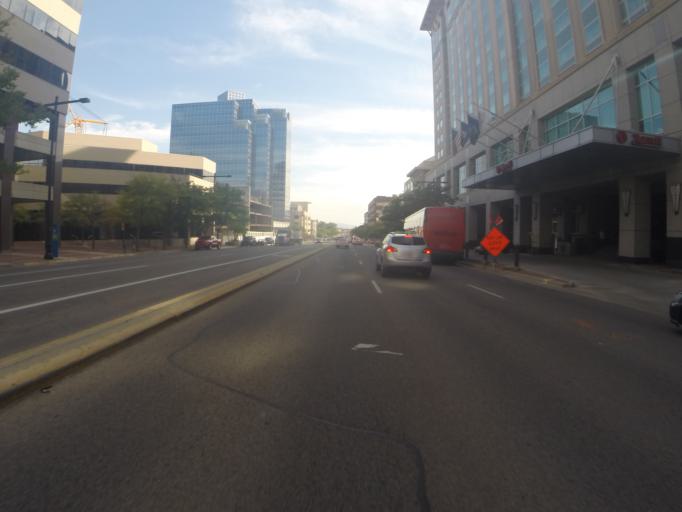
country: US
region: Utah
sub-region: Salt Lake County
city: Salt Lake City
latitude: 40.7647
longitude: -111.8883
